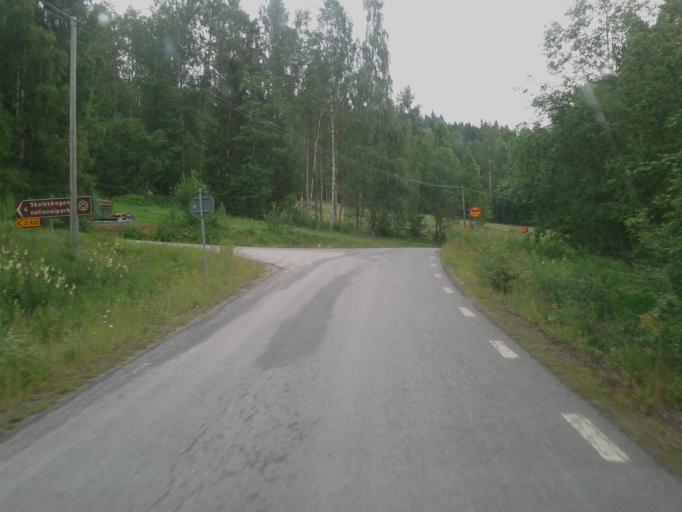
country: SE
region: Vaesternorrland
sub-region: OErnskoeldsviks Kommun
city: Bjasta
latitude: 63.0665
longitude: 18.4266
